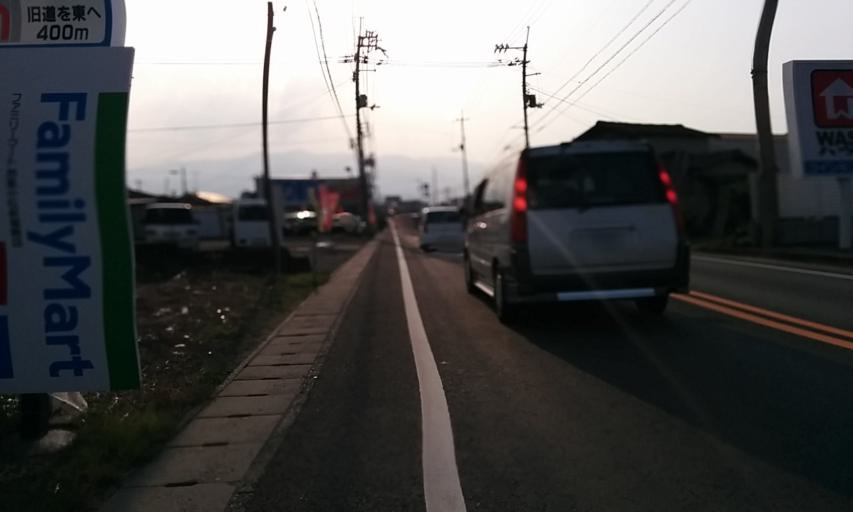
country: JP
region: Ehime
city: Saijo
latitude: 33.8964
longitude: 133.1223
